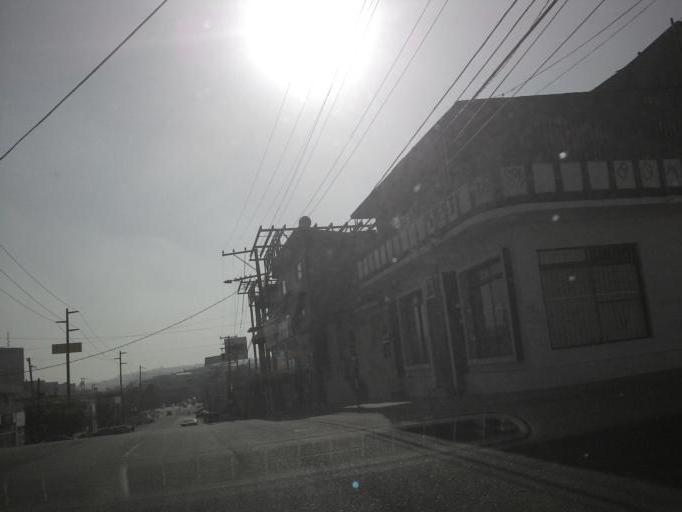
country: MX
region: Baja California
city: Tijuana
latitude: 32.5249
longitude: -117.0270
